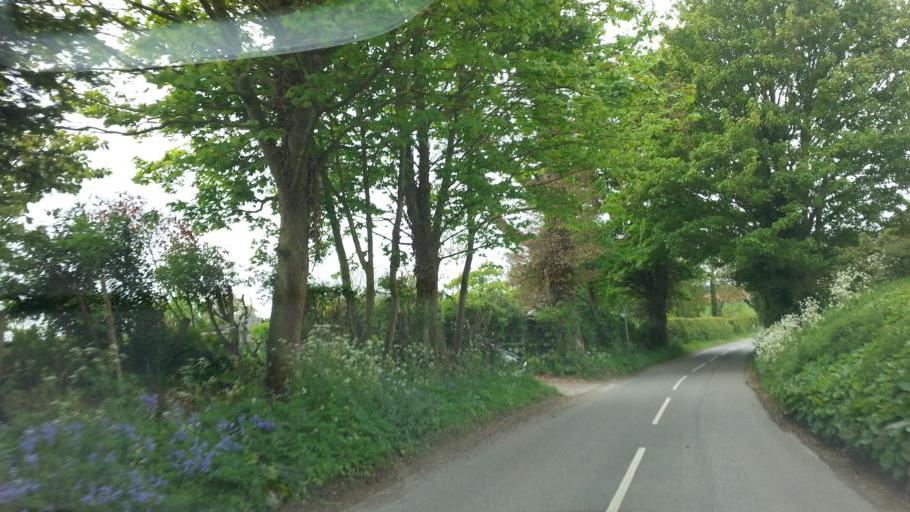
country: GB
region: England
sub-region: District of Rutland
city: Clipsham
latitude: 52.8603
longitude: -0.5070
